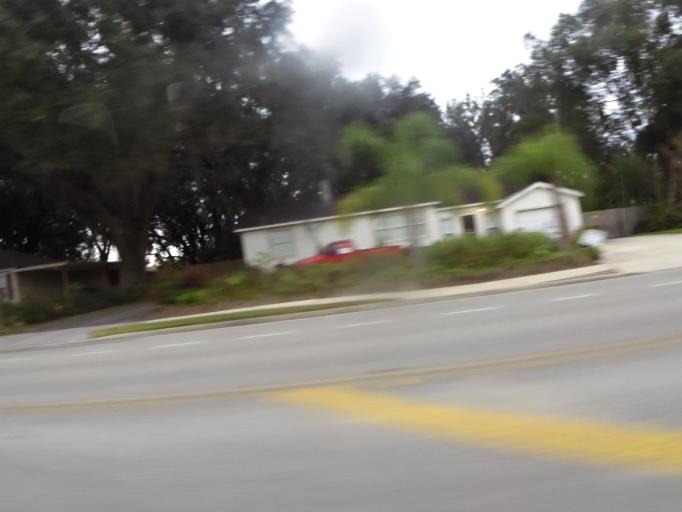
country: US
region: Florida
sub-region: Duval County
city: Jacksonville
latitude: 30.2643
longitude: -81.5945
